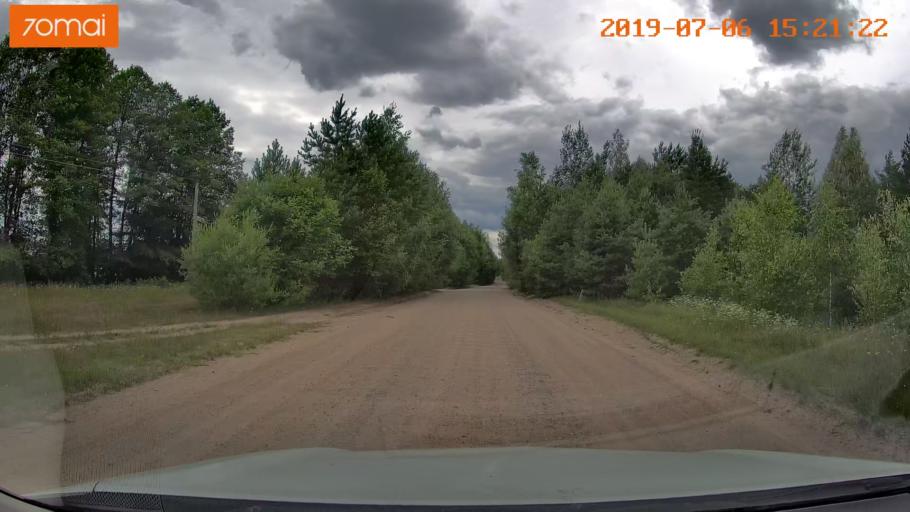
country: BY
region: Minsk
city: Valozhyn
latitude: 54.0104
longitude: 26.6157
